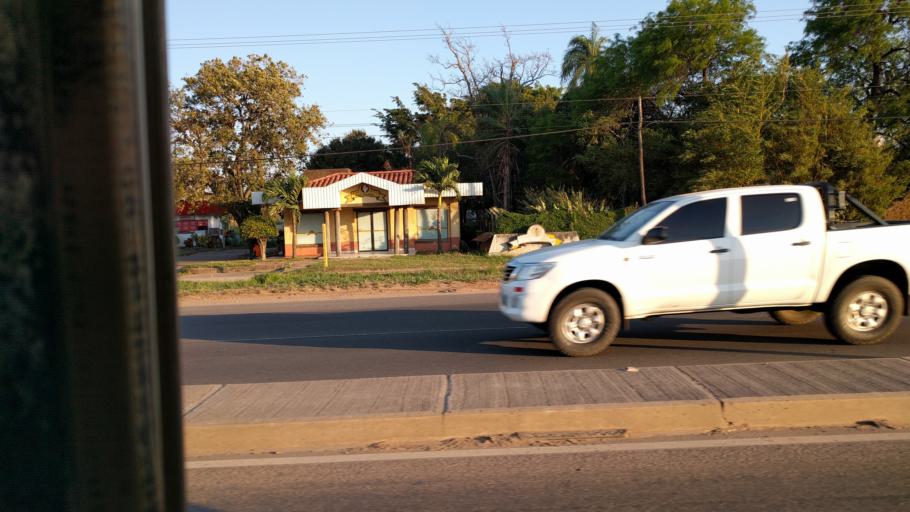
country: BO
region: Santa Cruz
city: Cotoca
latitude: -17.7668
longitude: -63.0503
